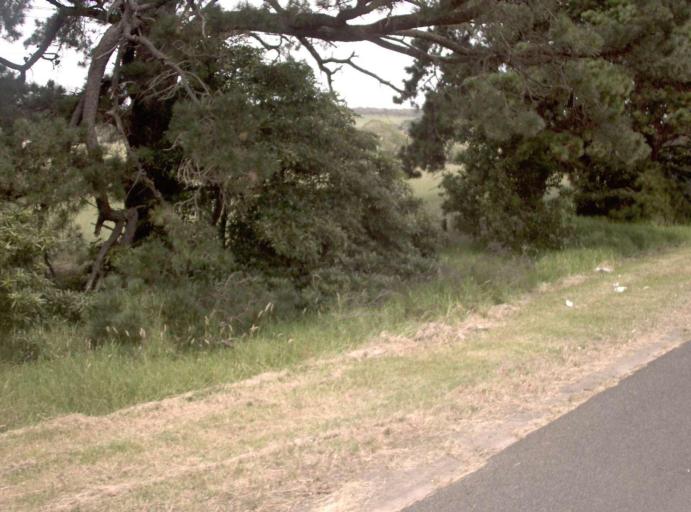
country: AU
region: Victoria
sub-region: Mornington Peninsula
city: Mornington
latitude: -38.2622
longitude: 145.0749
